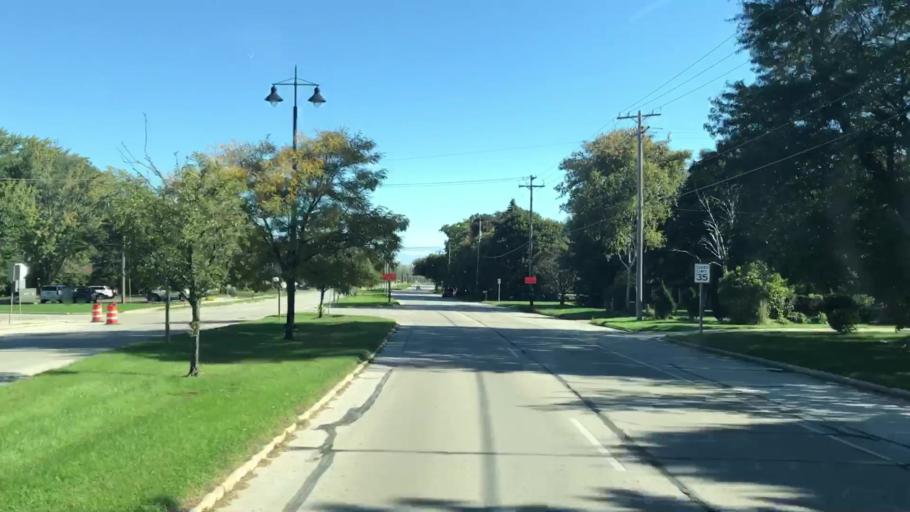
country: US
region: Wisconsin
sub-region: Milwaukee County
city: Hales Corners
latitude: 42.9391
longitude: -88.0437
